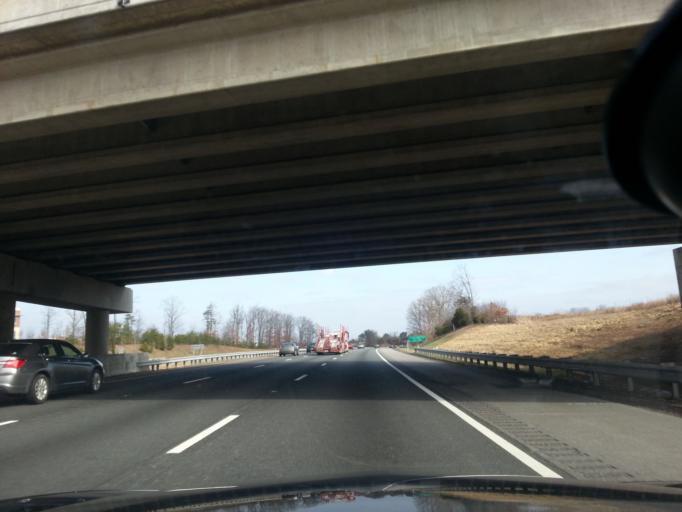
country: US
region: Virginia
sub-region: Spotsylvania County
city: Spotsylvania Courthouse
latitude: 38.2193
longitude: -77.4995
